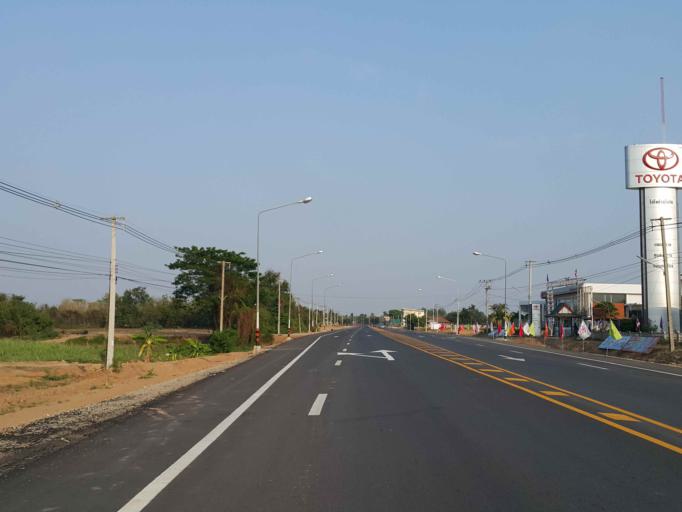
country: TH
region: Sukhothai
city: Sawankhalok
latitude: 17.3072
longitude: 99.8181
